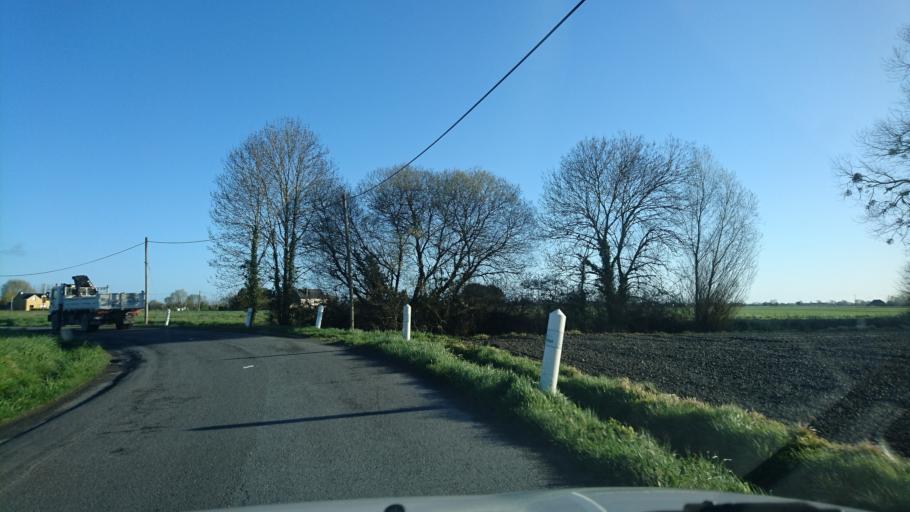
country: FR
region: Brittany
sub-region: Departement d'Ille-et-Vilaine
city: Cherrueix
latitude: 48.5878
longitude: -1.7181
